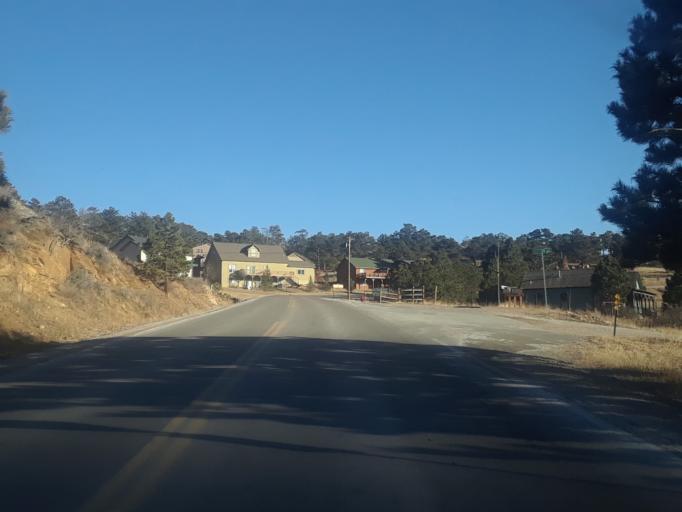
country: US
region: Colorado
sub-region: Larimer County
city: Estes Park
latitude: 40.3511
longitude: -105.5405
